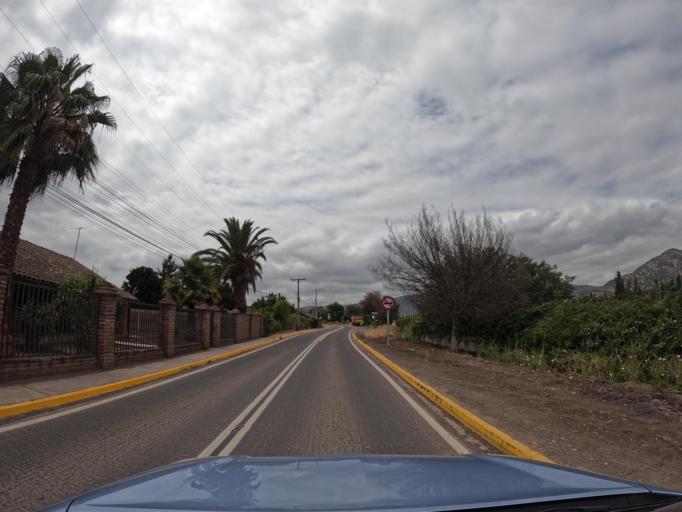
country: CL
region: Maule
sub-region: Provincia de Curico
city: Teno
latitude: -34.7702
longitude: -71.1894
